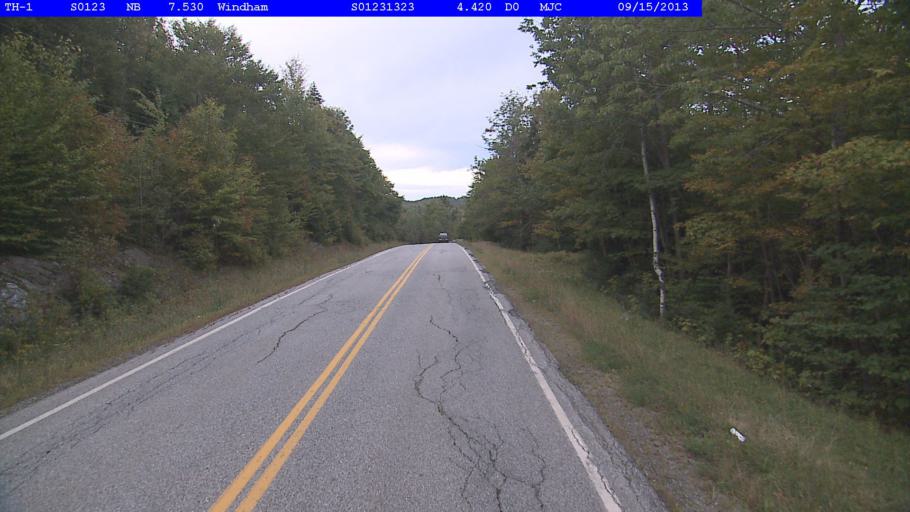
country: US
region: Vermont
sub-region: Windsor County
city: Chester
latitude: 43.1870
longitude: -72.7211
